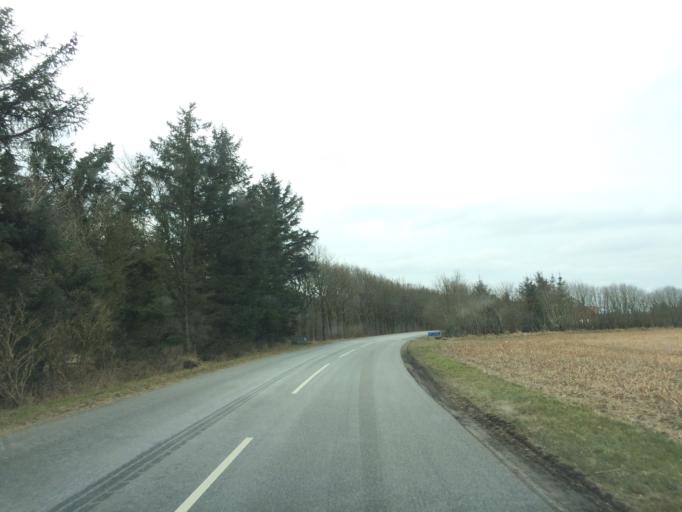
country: DK
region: Central Jutland
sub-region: Ringkobing-Skjern Kommune
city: Tarm
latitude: 55.8032
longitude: 8.3837
